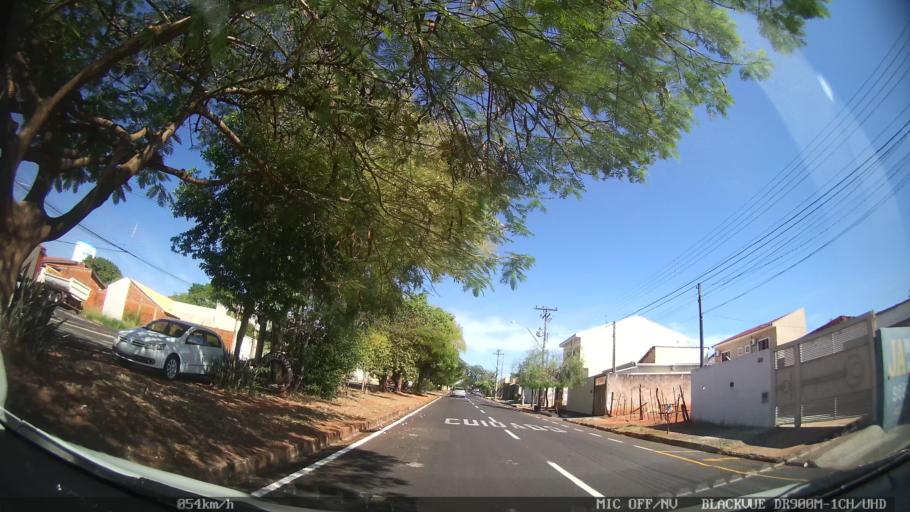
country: BR
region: Sao Paulo
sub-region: Sao Jose Do Rio Preto
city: Sao Jose do Rio Preto
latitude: -20.7666
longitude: -49.4068
